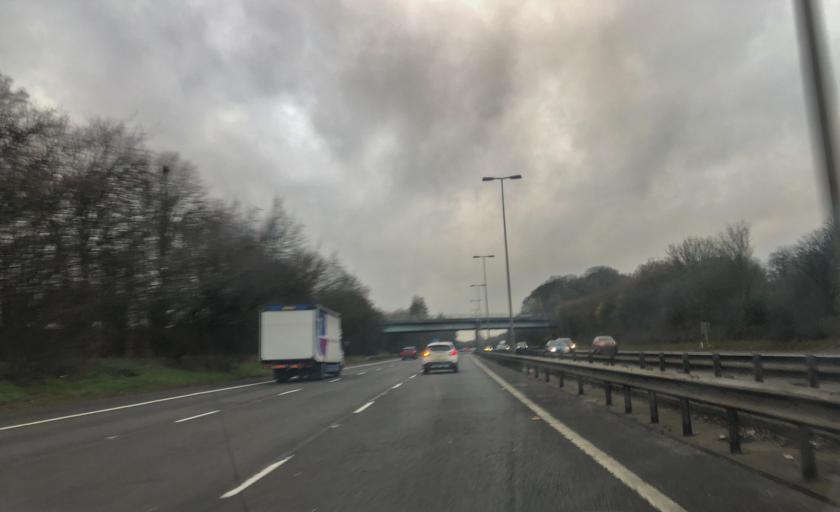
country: GB
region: England
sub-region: Buckinghamshire
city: Stokenchurch
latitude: 51.6447
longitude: -0.8897
